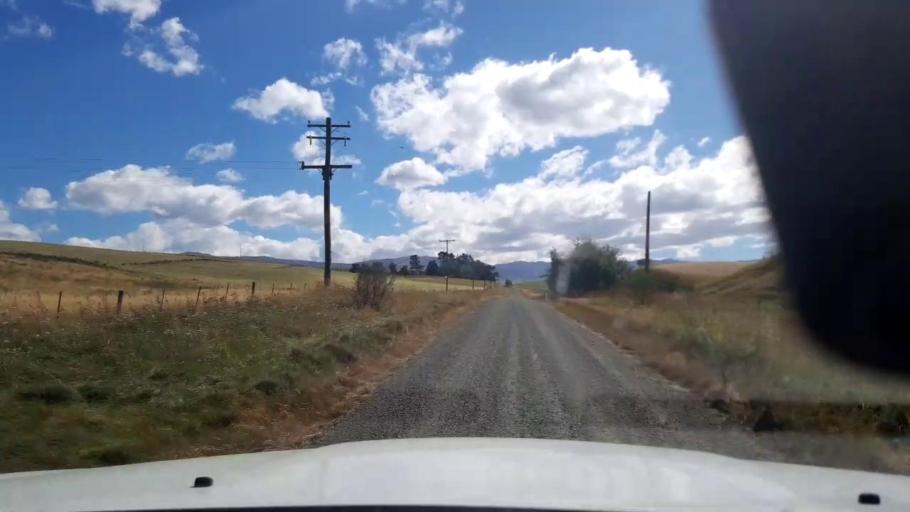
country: NZ
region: Canterbury
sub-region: Timaru District
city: Pleasant Point
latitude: -44.2391
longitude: 170.8632
